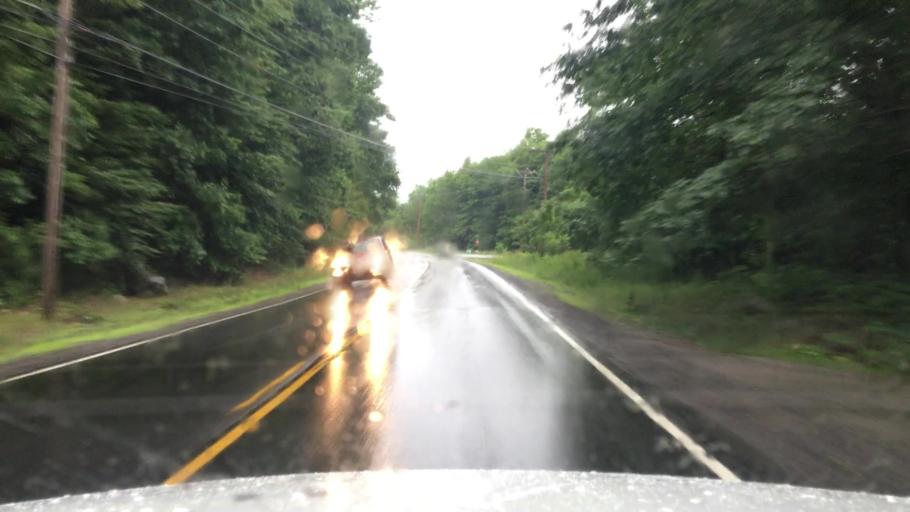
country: US
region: Maine
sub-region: Kennebec County
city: Manchester
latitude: 44.3115
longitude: -69.8354
